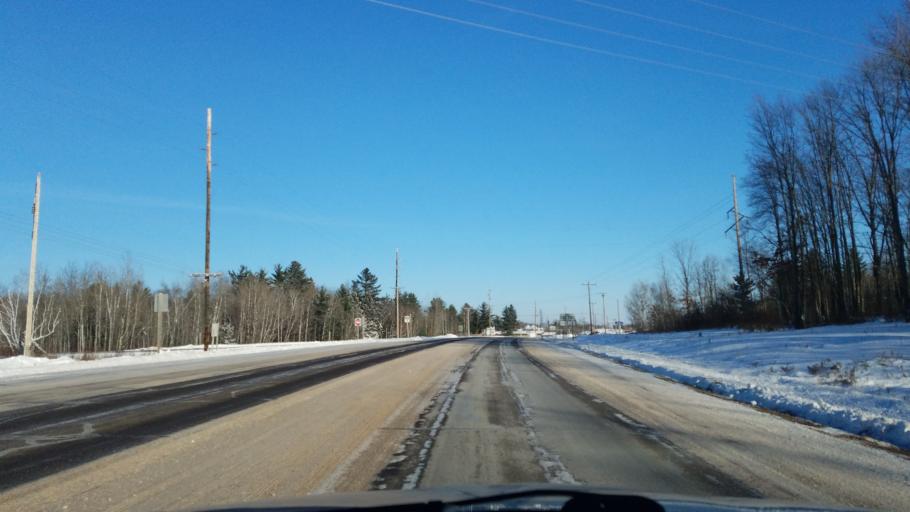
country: US
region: Wisconsin
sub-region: Barron County
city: Cumberland
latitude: 45.5302
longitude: -92.0441
